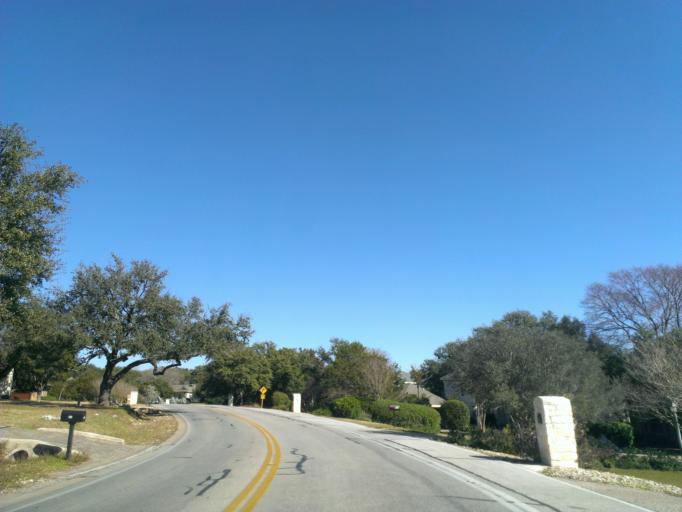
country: US
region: Texas
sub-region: Travis County
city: Lakeway
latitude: 30.3690
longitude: -97.9780
